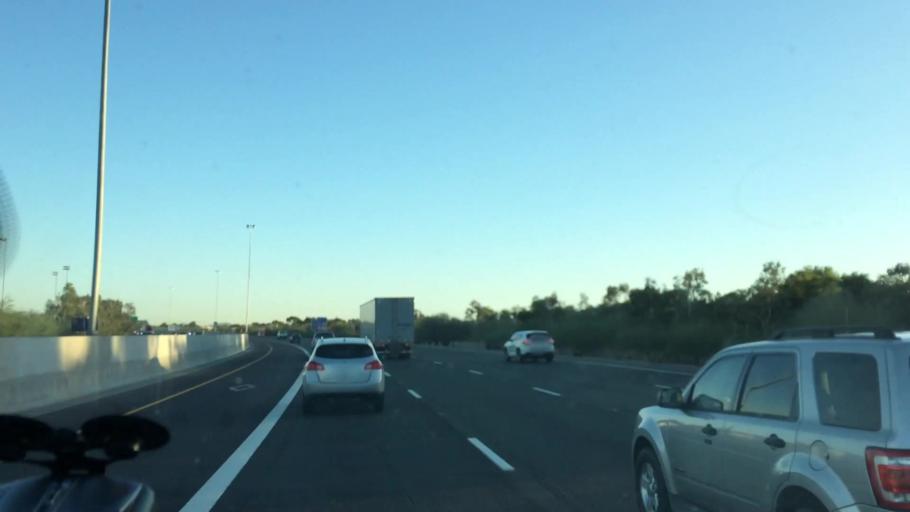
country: US
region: Arizona
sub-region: Maricopa County
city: Peoria
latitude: 33.6154
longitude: -112.2406
